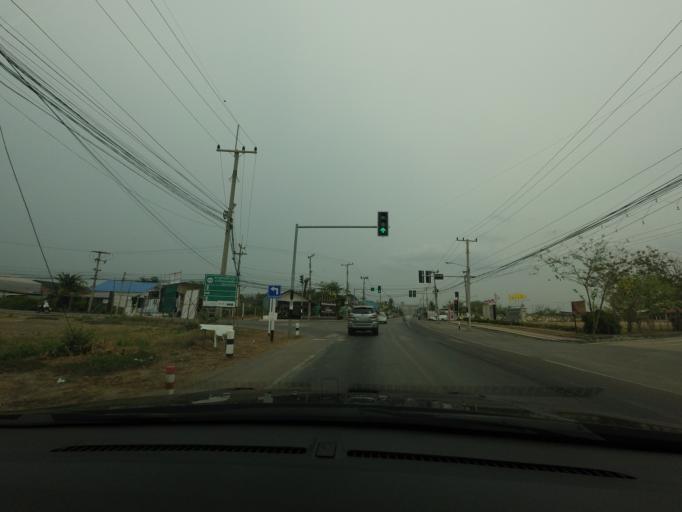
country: TH
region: Phetchaburi
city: Ban Laem
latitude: 13.2183
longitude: 99.9774
